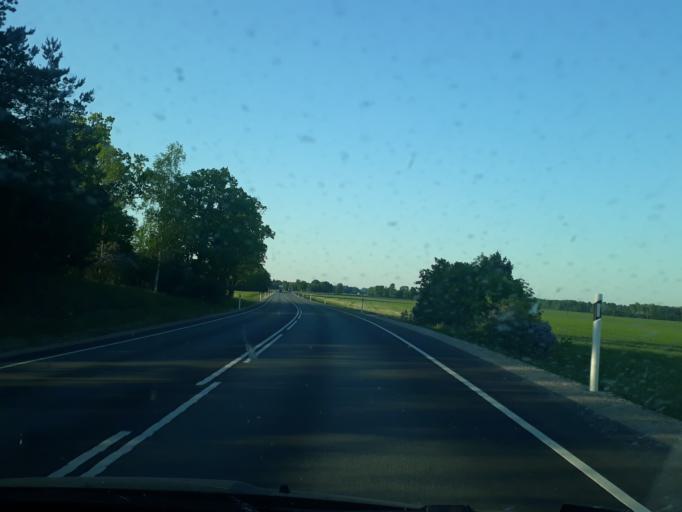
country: EE
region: Paernumaa
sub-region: Tootsi vald
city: Tootsi
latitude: 58.5448
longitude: 24.8455
